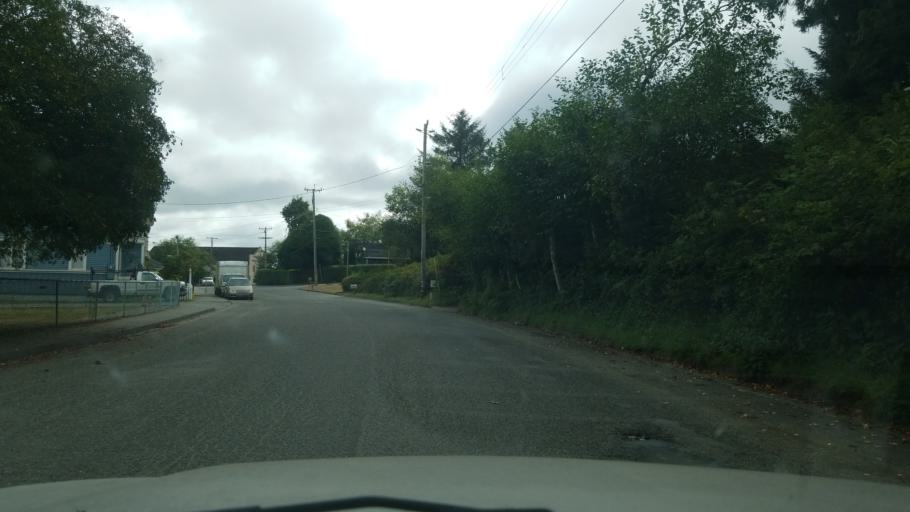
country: US
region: California
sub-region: Humboldt County
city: Ferndale
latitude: 40.5765
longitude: -124.2677
